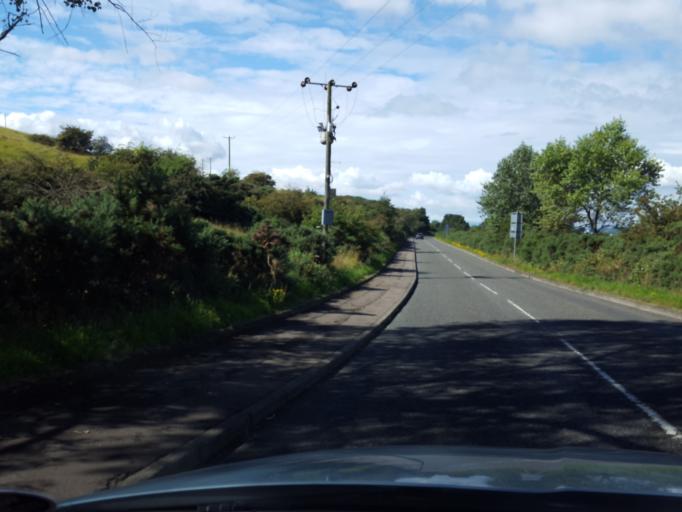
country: GB
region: Scotland
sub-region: Fife
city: North Queensferry
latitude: 56.0168
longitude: -3.3950
